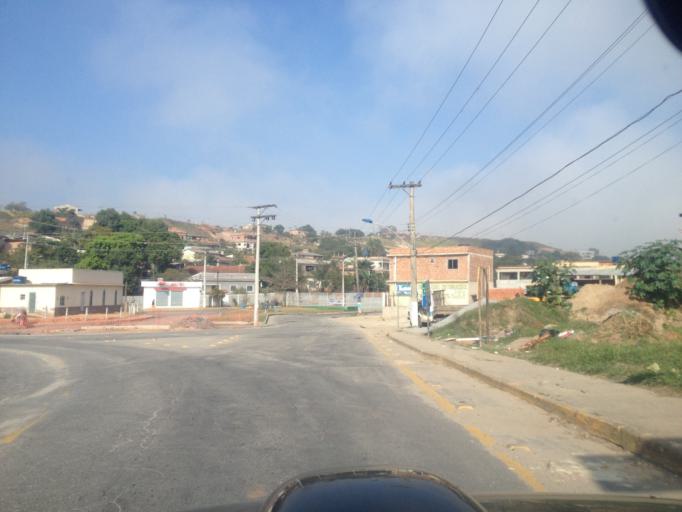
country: BR
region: Rio de Janeiro
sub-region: Porto Real
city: Porto Real
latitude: -22.4396
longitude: -44.3177
